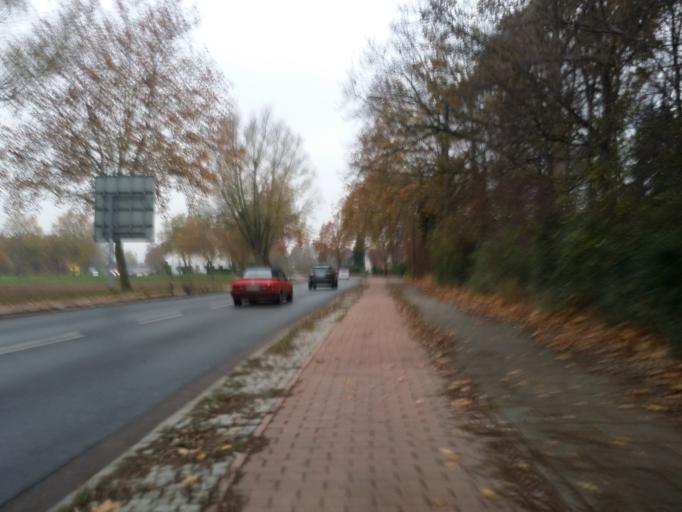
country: DE
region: Bremen
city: Bremen
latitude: 53.0371
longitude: 8.8362
